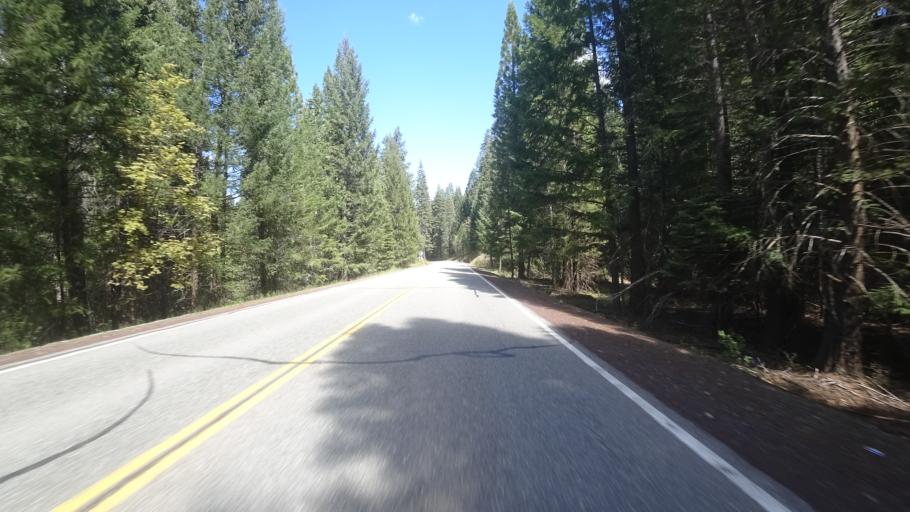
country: US
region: California
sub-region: Trinity County
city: Weaverville
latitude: 40.8276
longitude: -122.8844
